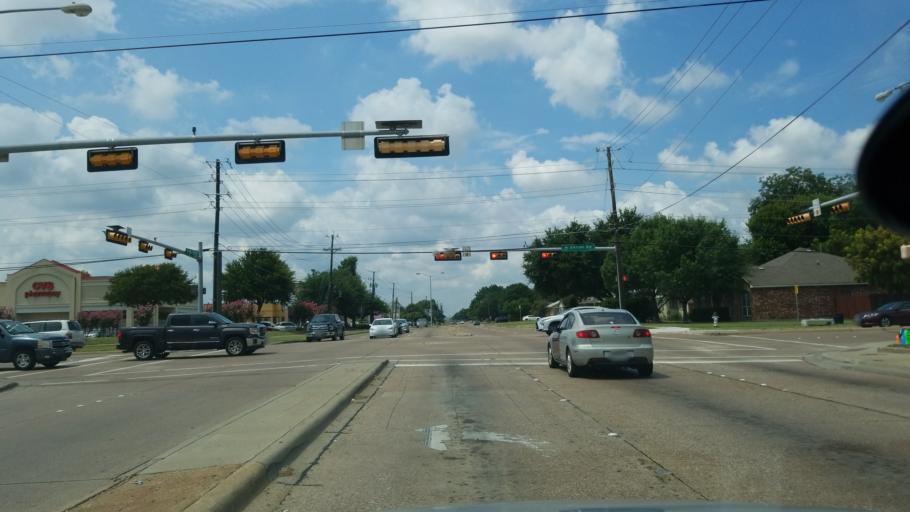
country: US
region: Texas
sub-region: Dallas County
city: Garland
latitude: 32.9164
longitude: -96.6649
